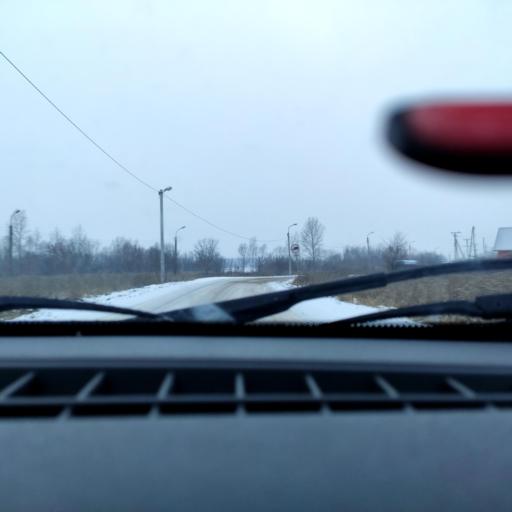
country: RU
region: Bashkortostan
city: Blagoveshchensk
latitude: 54.8891
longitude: 56.0372
